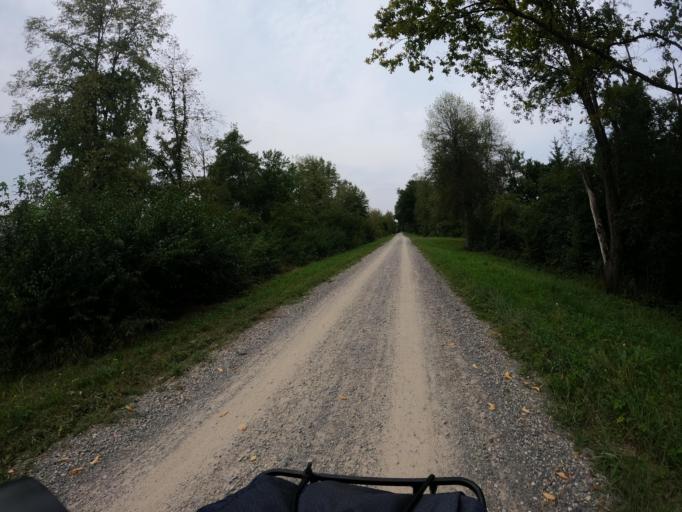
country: CH
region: Zurich
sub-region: Bezirk Affoltern
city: Ottenbach
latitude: 47.2736
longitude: 8.3978
